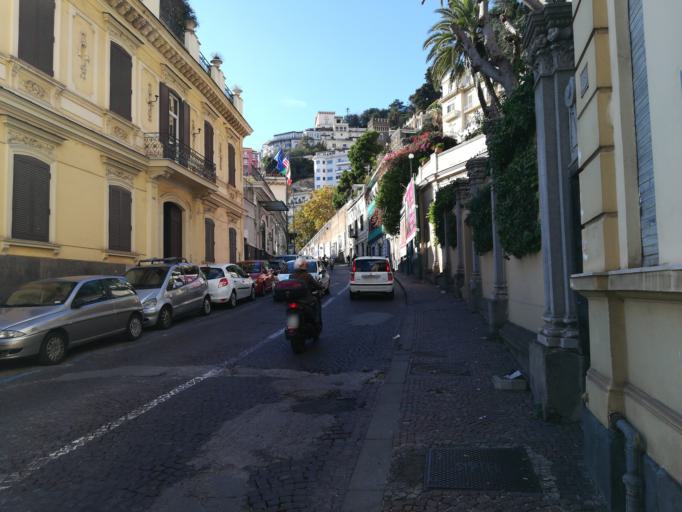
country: IT
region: Campania
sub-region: Provincia di Napoli
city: Napoli
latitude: 40.8385
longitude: 14.2351
